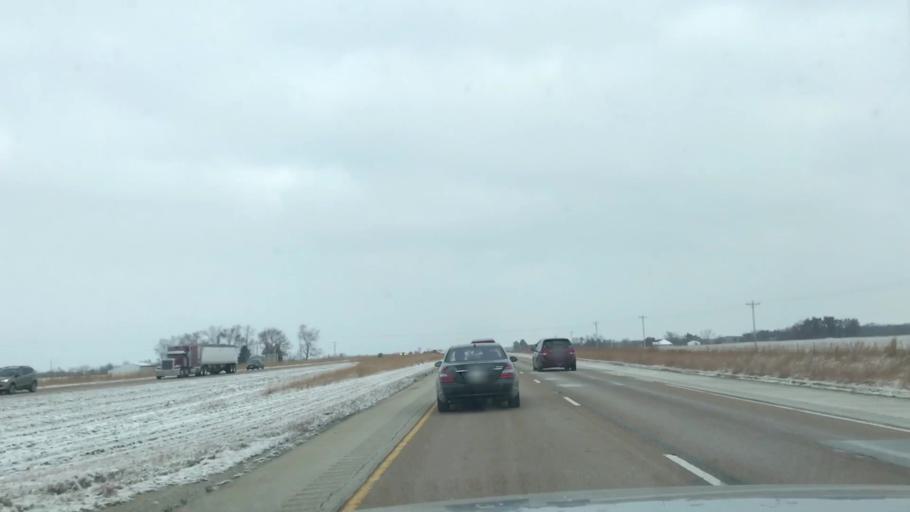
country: US
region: Illinois
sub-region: Montgomery County
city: Litchfield
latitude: 39.2382
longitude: -89.6411
